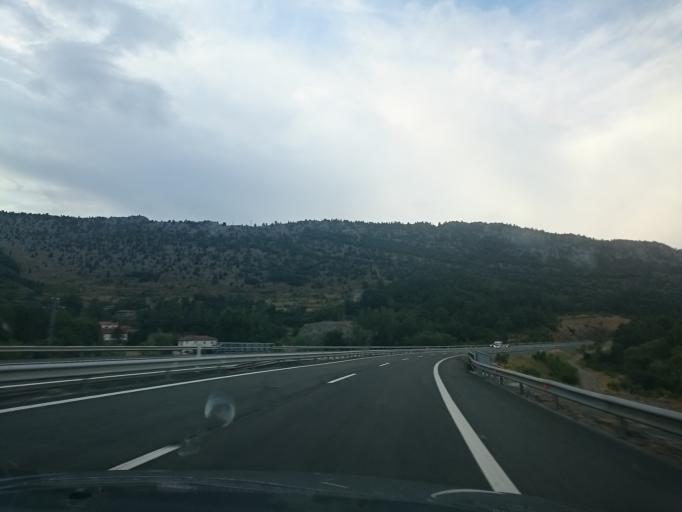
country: ES
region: Castille and Leon
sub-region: Provincia de Leon
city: Sena de Luna
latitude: 42.8704
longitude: -5.8858
